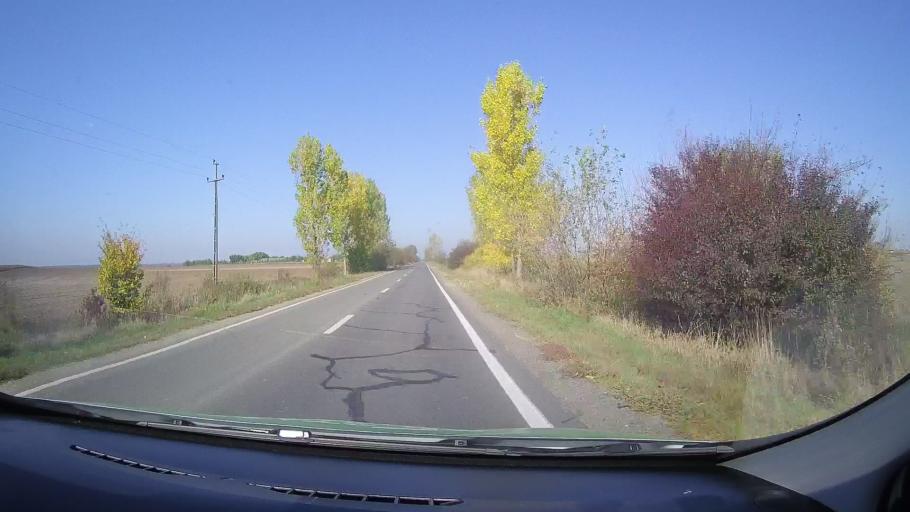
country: RO
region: Satu Mare
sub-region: Comuna Urziceni
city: Urziceni
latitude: 47.7175
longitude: 22.4198
